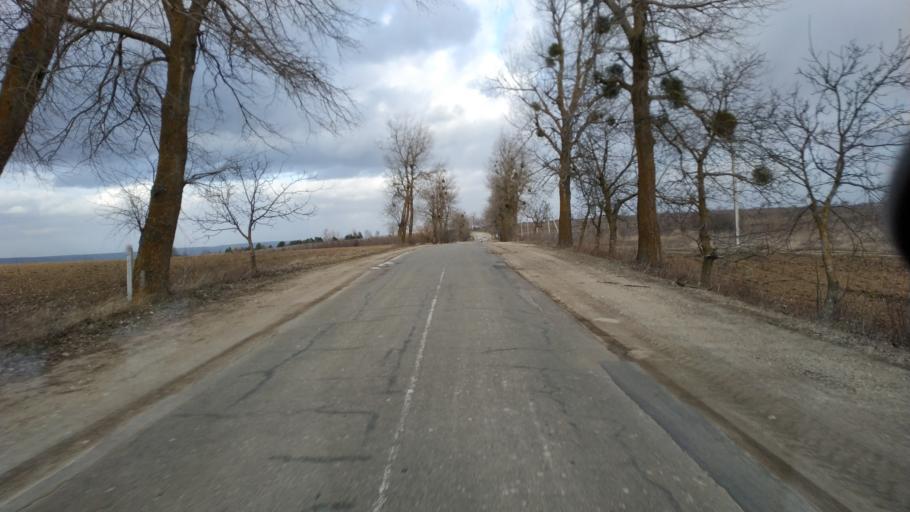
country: MD
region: Calarasi
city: Calarasi
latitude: 47.2866
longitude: 28.3504
